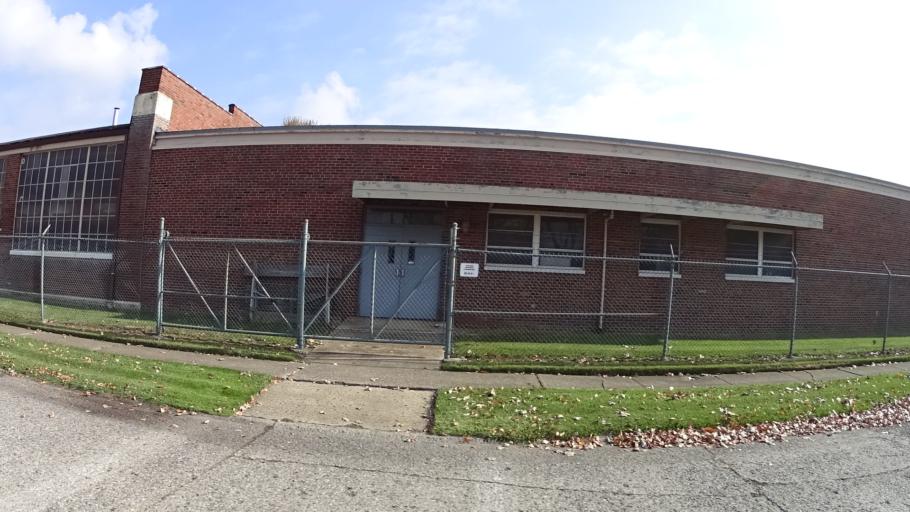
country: US
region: Ohio
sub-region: Lorain County
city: Elyria
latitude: 41.3705
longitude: -82.0817
